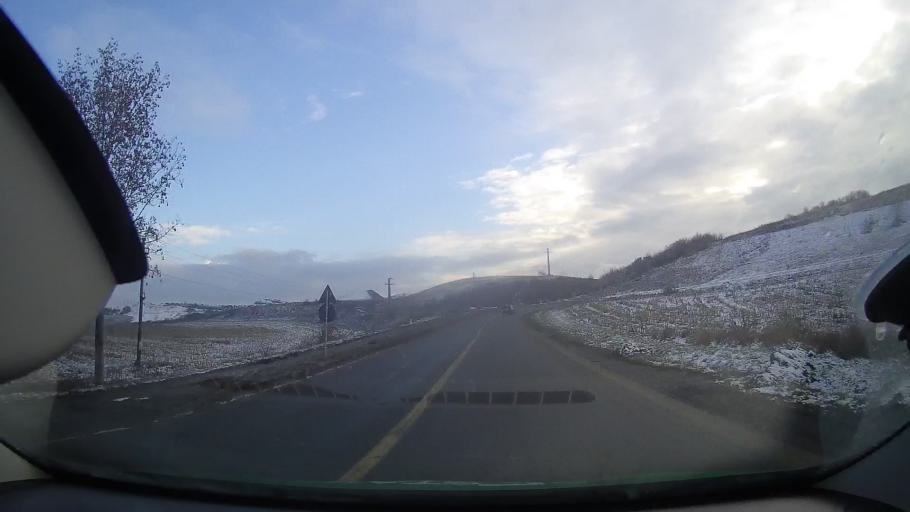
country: RO
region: Mures
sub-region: Comuna Iernut
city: Iernut
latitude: 46.4294
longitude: 24.2595
